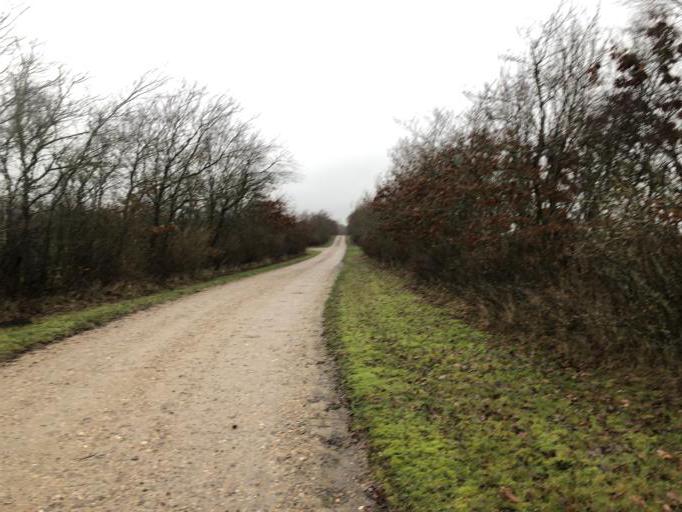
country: DK
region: Central Jutland
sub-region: Holstebro Kommune
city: Ulfborg
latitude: 56.3009
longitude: 8.4475
